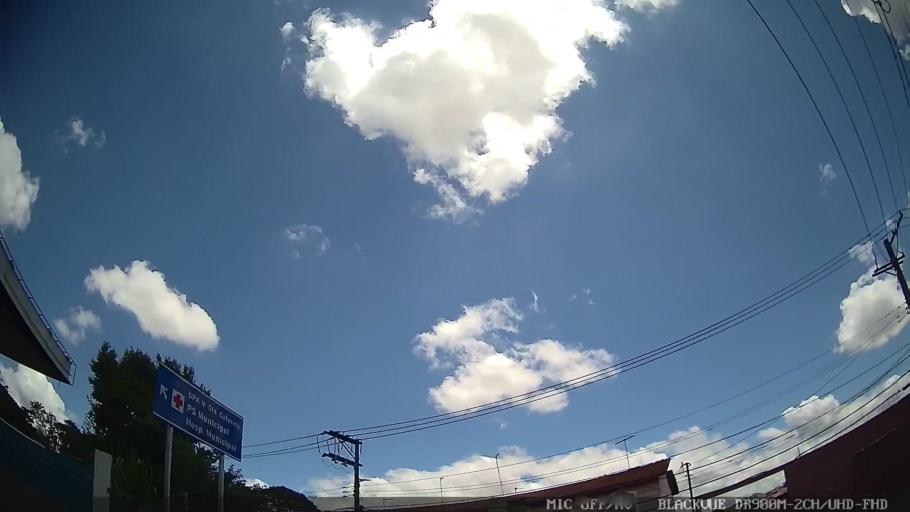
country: BR
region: Sao Paulo
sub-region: Diadema
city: Diadema
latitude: -23.6611
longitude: -46.6605
